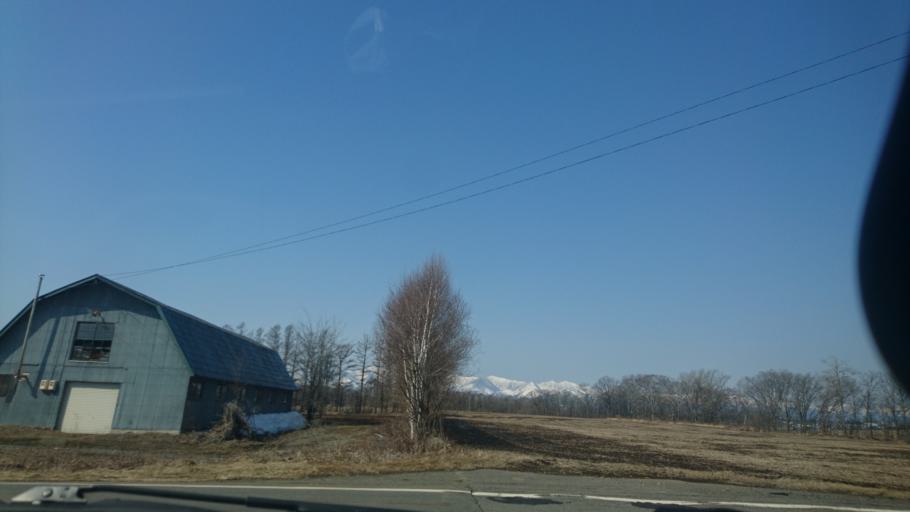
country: JP
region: Hokkaido
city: Obihiro
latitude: 42.9099
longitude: 143.0705
